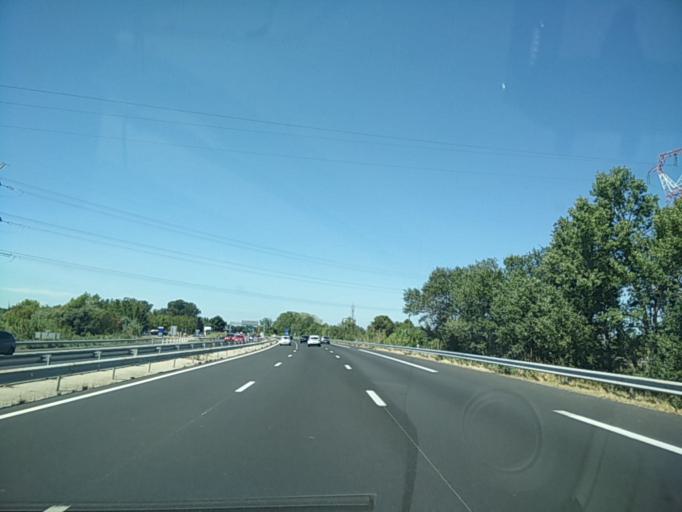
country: FR
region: Provence-Alpes-Cote d'Azur
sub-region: Departement du Vaucluse
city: Cavaillon
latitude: 43.8284
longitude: 5.0202
